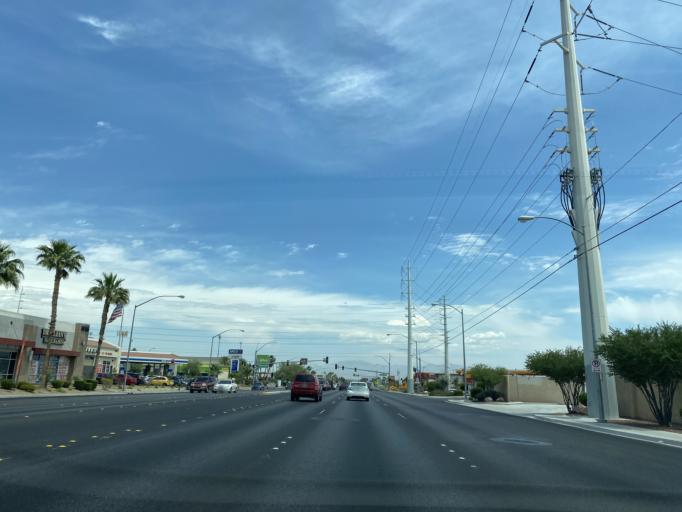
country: US
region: Nevada
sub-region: Clark County
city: Spring Valley
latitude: 36.0837
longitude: -115.2427
